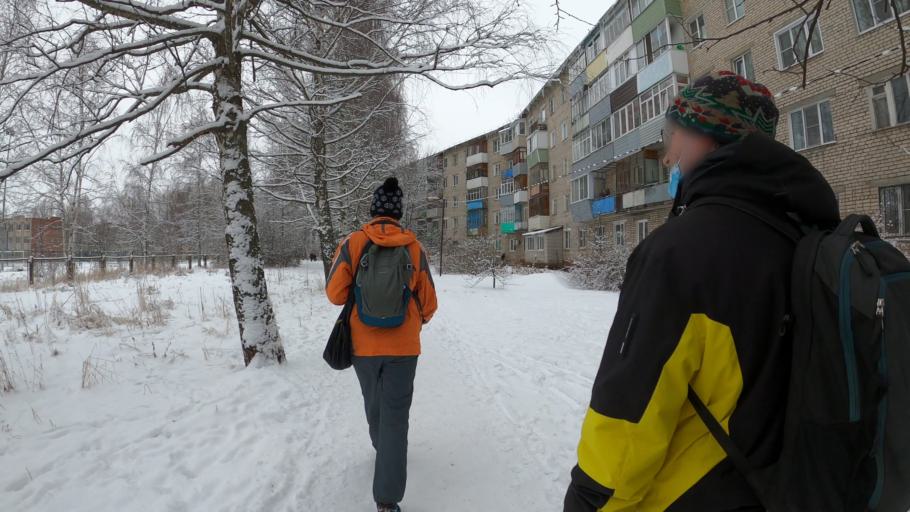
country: RU
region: Jaroslavl
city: Pereslavl'-Zalesskiy
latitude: 56.7539
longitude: 38.8709
